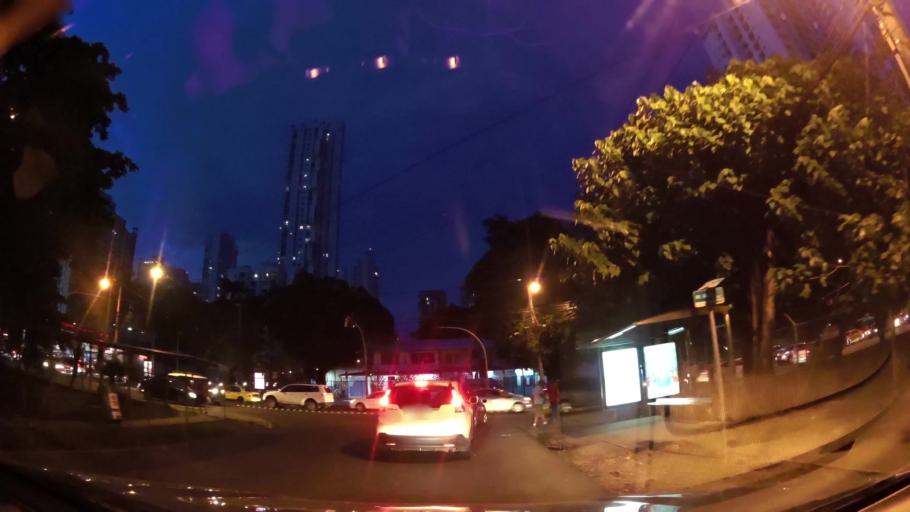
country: PA
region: Panama
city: Panama
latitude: 8.9873
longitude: -79.5041
